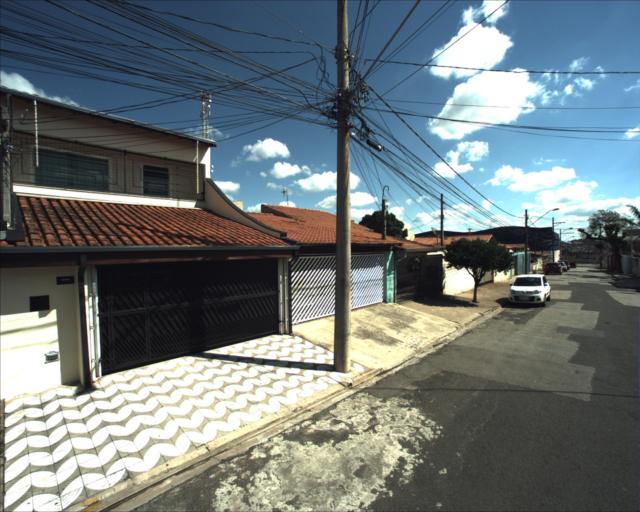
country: BR
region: Sao Paulo
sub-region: Sorocaba
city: Sorocaba
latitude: -23.4761
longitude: -47.4737
